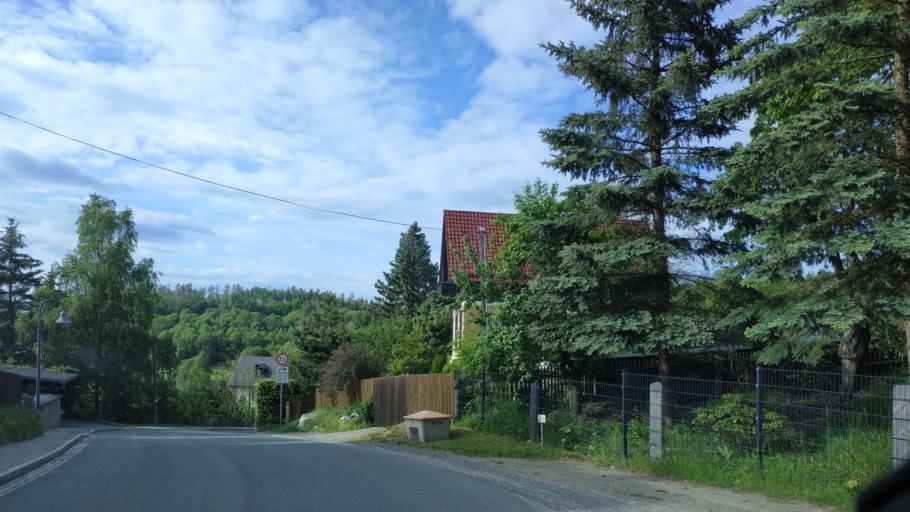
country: DE
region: Saxony
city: Pohl
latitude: 50.5578
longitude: 12.1838
